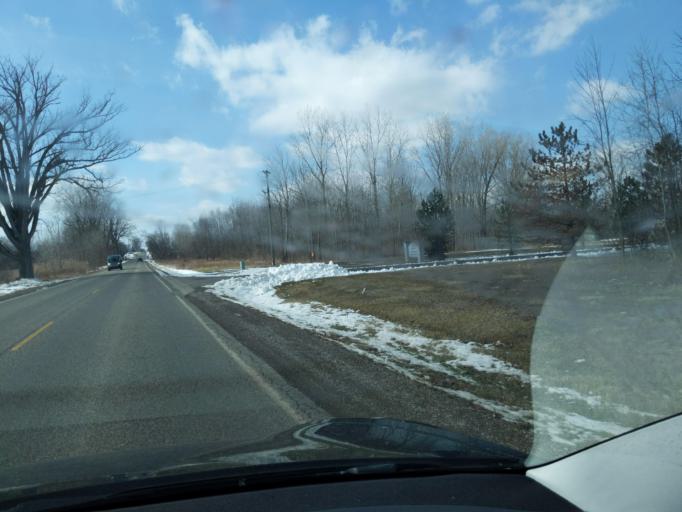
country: US
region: Michigan
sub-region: Livingston County
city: Fowlerville
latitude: 42.6430
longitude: -84.0774
